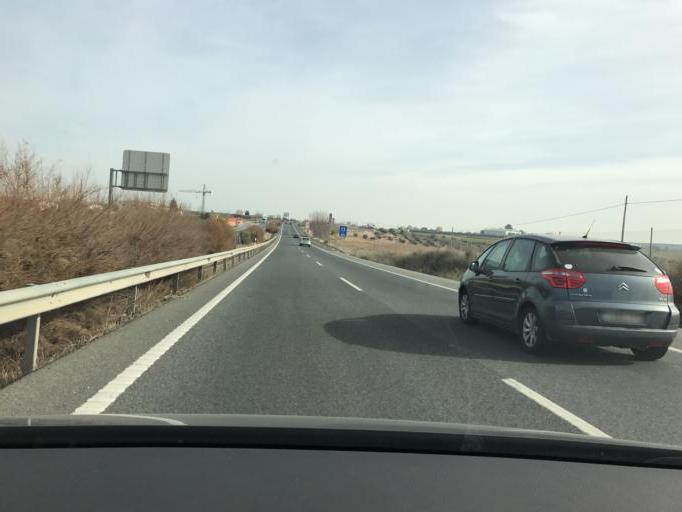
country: ES
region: Andalusia
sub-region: Provincia de Granada
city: Moraleda de Zafayona
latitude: 37.1799
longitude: -3.9399
